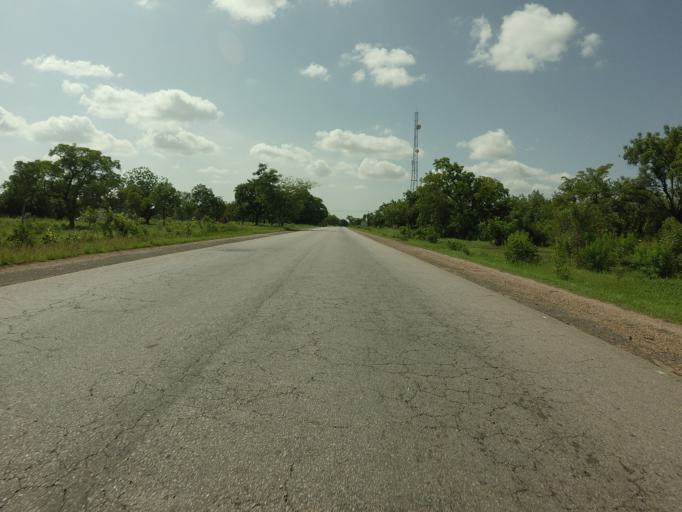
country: GH
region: Northern
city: Savelugu
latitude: 9.8163
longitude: -0.8623
